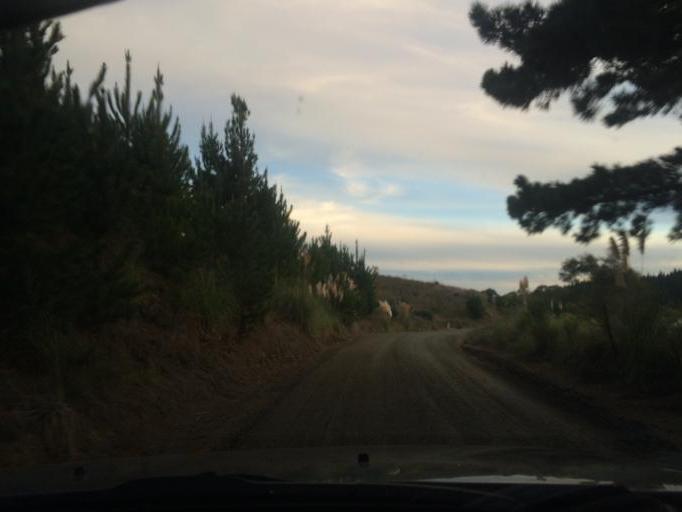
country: NZ
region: Northland
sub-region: Whangarei
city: Maungatapere
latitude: -35.8094
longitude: 174.0411
